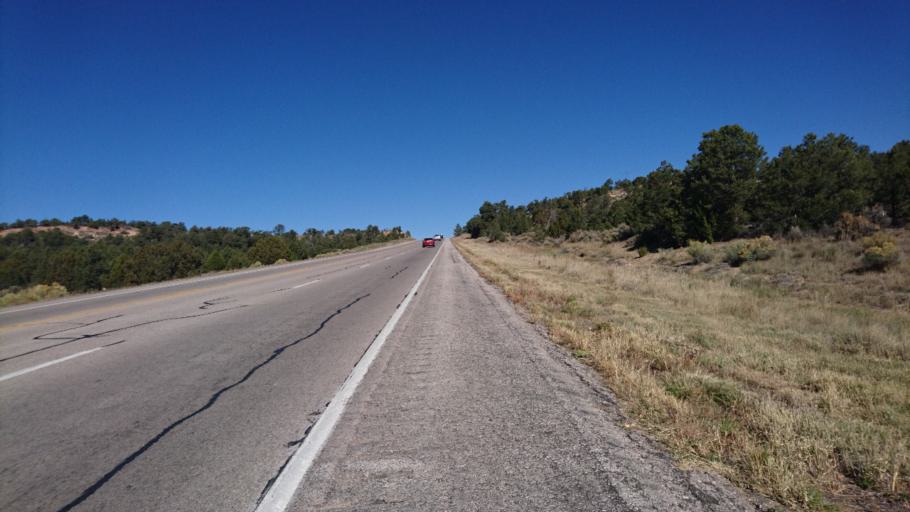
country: US
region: New Mexico
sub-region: McKinley County
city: Black Rock
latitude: 35.2164
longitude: -108.7637
